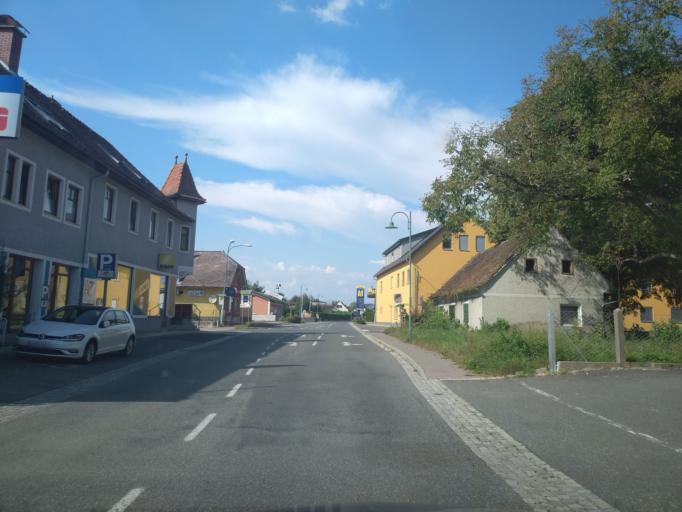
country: AT
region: Styria
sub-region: Politischer Bezirk Leibnitz
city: Kaindorf an der Sulm
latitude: 46.7932
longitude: 15.5383
